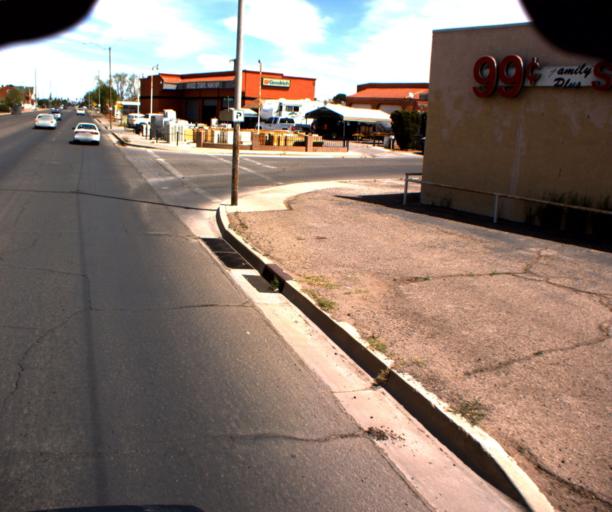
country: US
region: Arizona
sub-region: Cochise County
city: Douglas
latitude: 31.3411
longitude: -109.5582
